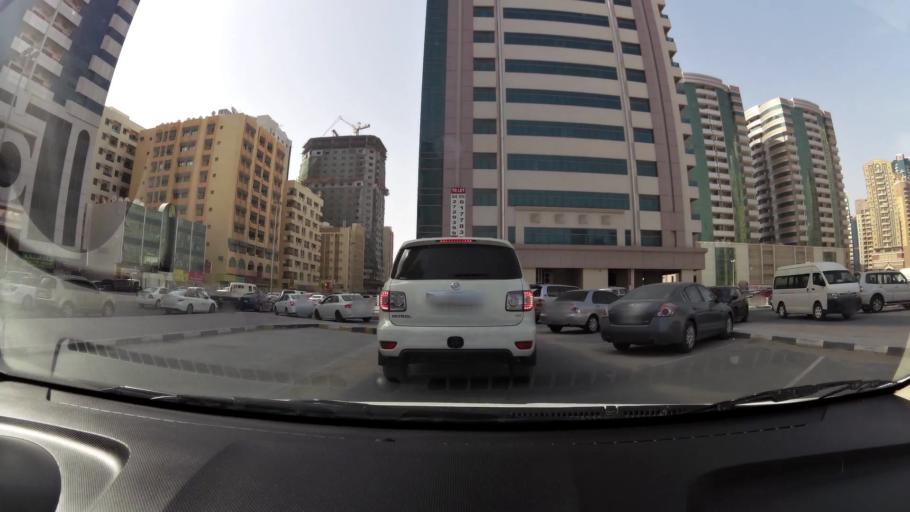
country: AE
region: Ash Shariqah
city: Sharjah
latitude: 25.3187
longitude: 55.3797
